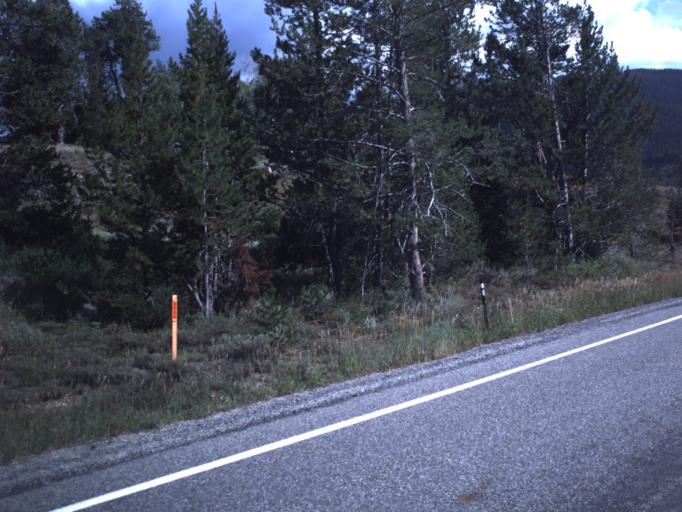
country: US
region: Utah
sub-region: Cache County
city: Richmond
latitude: 41.9688
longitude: -111.5320
